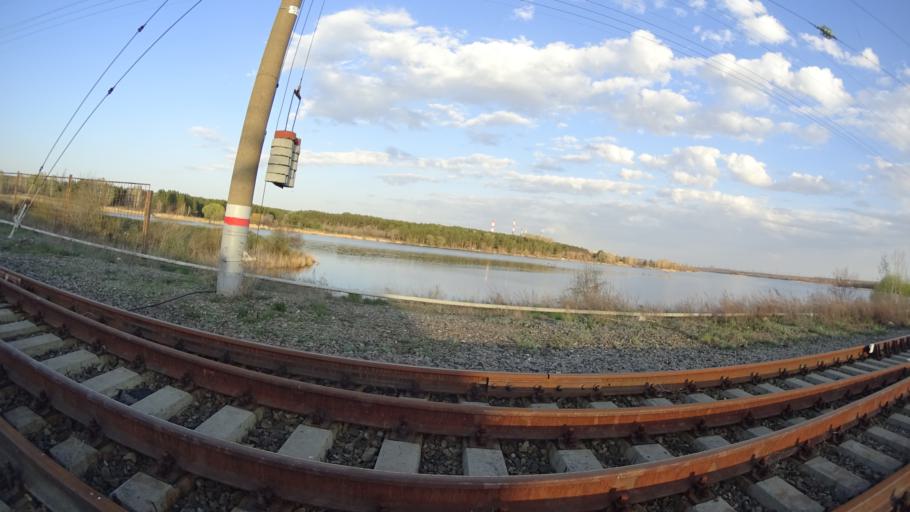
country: RU
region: Chelyabinsk
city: Troitsk
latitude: 54.0543
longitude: 61.6104
